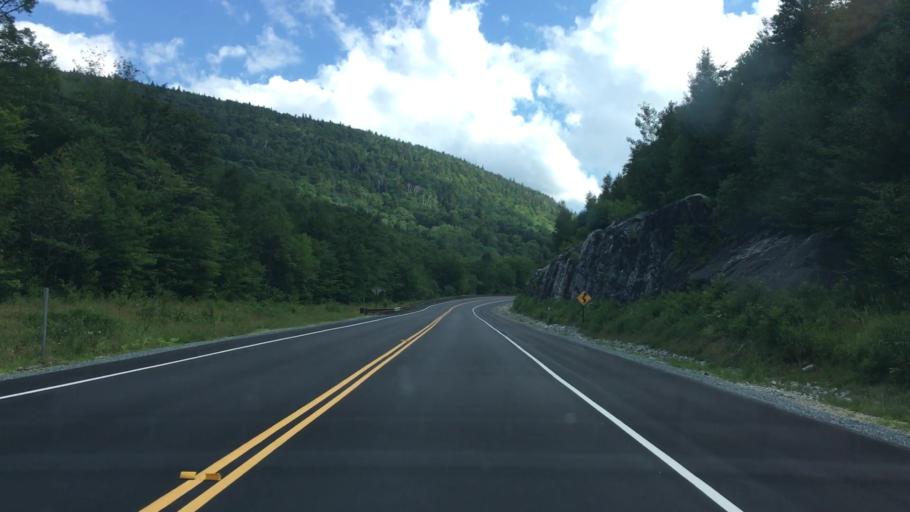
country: US
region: New Hampshire
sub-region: Grafton County
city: Woodstock
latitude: 44.0542
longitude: -71.7938
